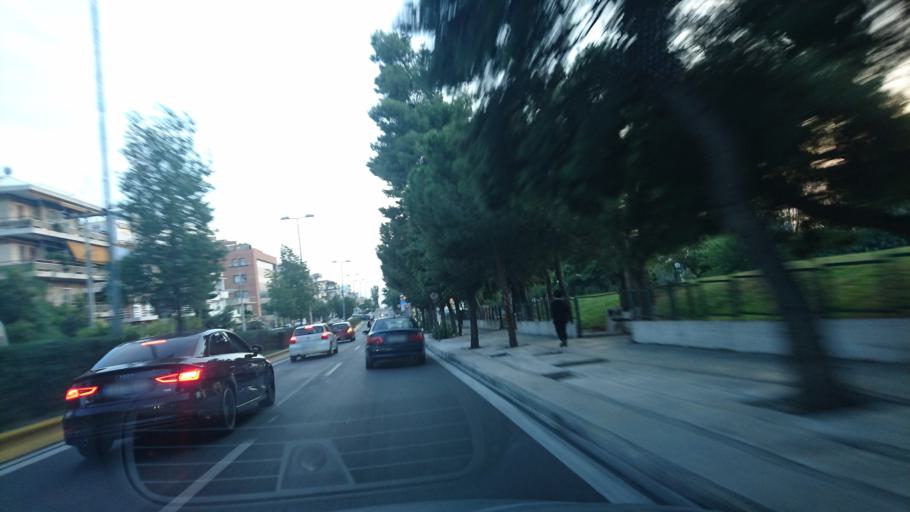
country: GR
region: Attica
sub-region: Nomarchia Athinas
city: Ilioupoli
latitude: 37.9403
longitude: 23.7611
